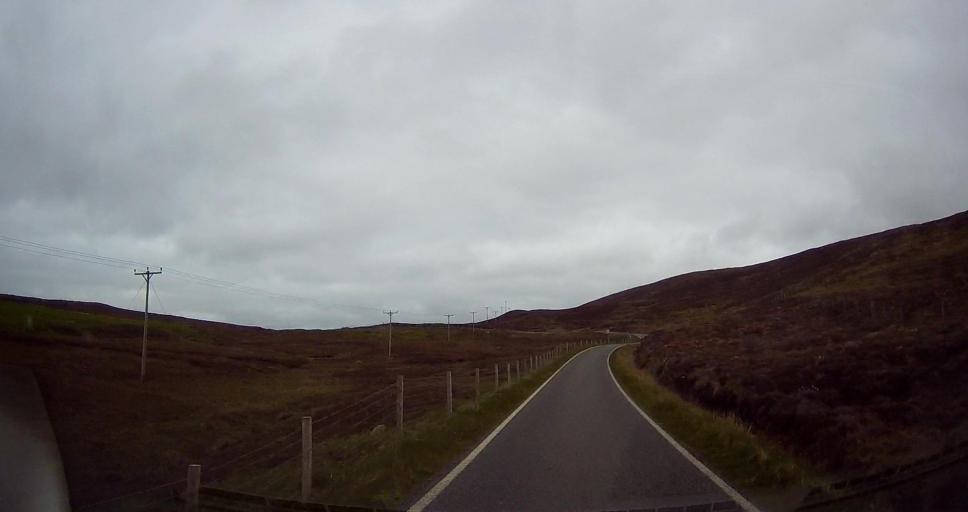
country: GB
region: Scotland
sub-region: Shetland Islands
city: Lerwick
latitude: 60.3078
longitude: -1.3382
